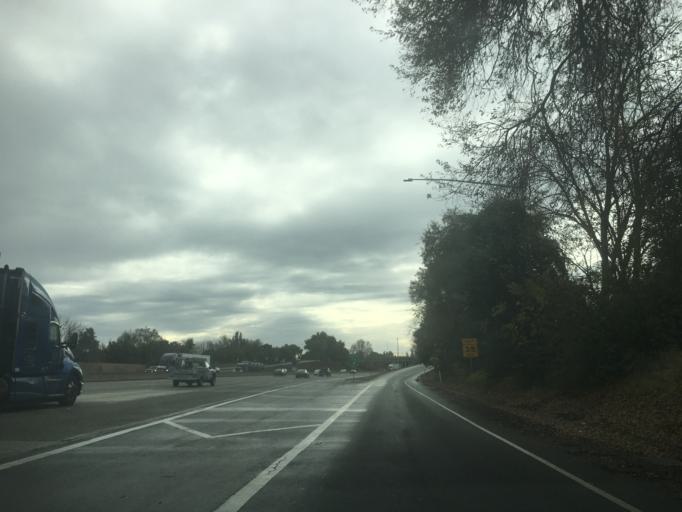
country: US
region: California
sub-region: Sacramento County
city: Sacramento
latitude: 38.5439
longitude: -121.5086
